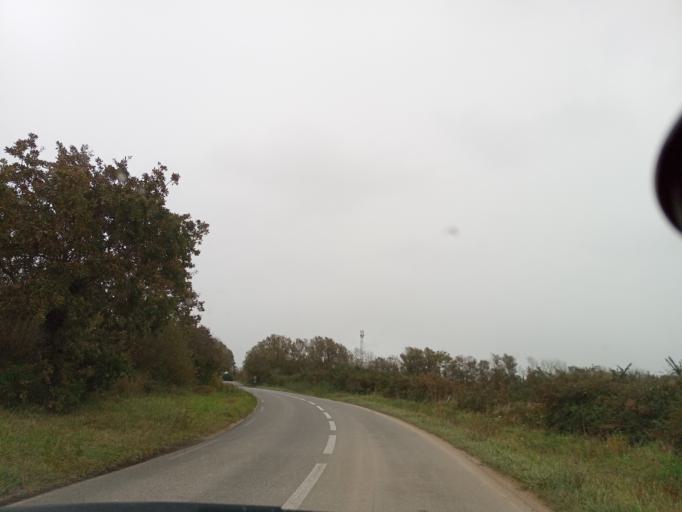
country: FR
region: Brittany
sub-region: Departement du Finistere
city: Esquibien
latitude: 48.0184
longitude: -4.5625
